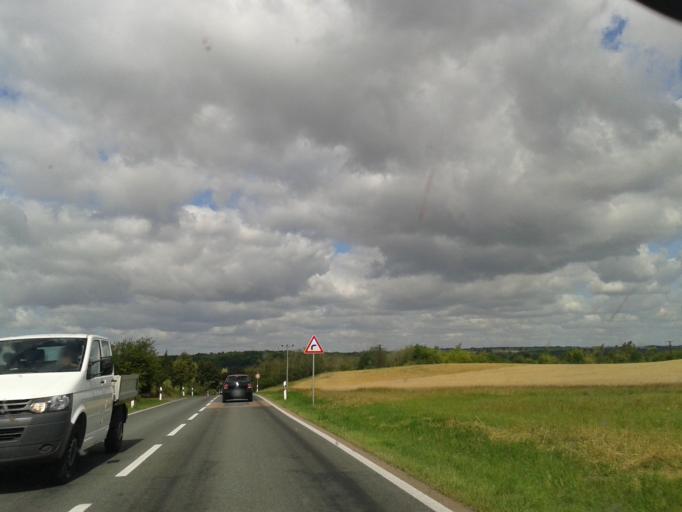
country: DE
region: Saxony-Anhalt
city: Salzmunde
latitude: 51.5237
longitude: 11.8409
